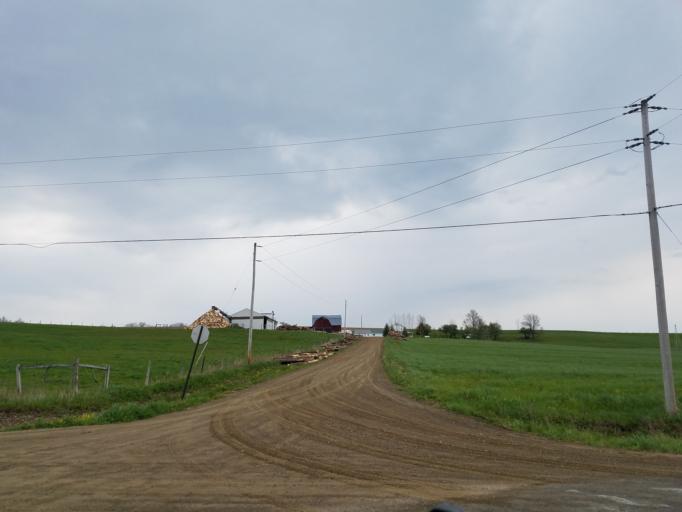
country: US
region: New York
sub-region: Steuben County
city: Canisteo
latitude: 42.1443
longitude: -77.5503
